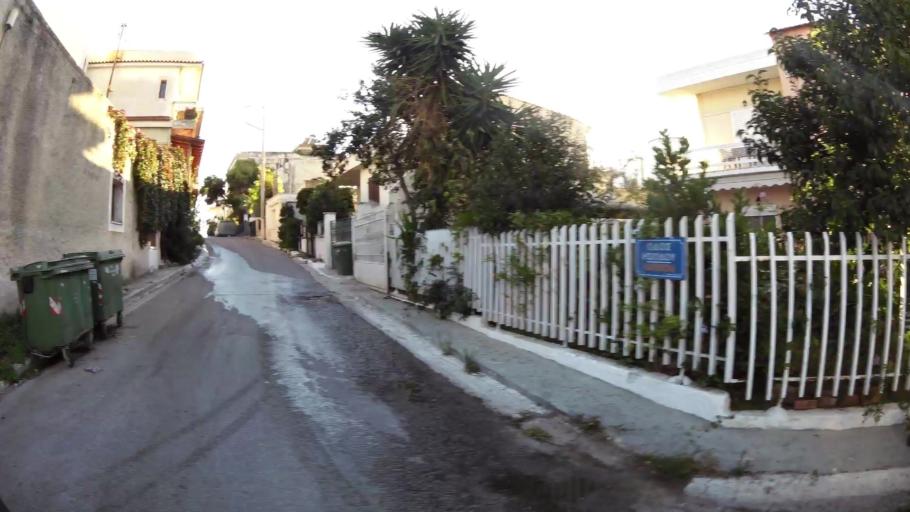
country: GR
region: Attica
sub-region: Nomarchia Anatolikis Attikis
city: Spata
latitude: 37.9605
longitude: 23.9117
